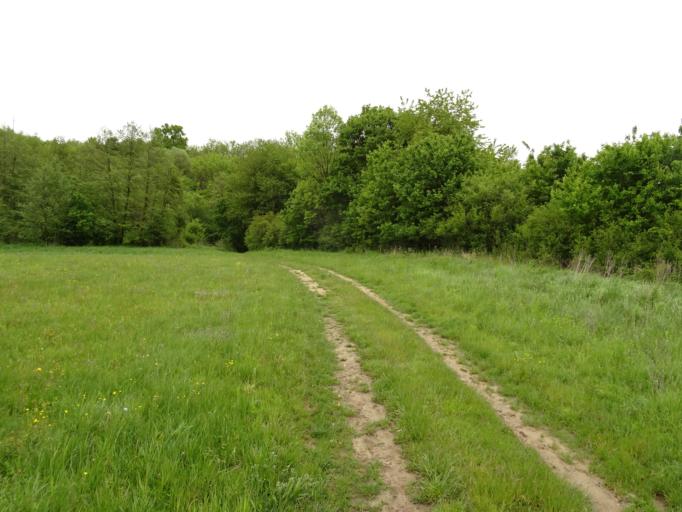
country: HU
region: Veszprem
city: Urkut
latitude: 47.1575
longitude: 17.6726
